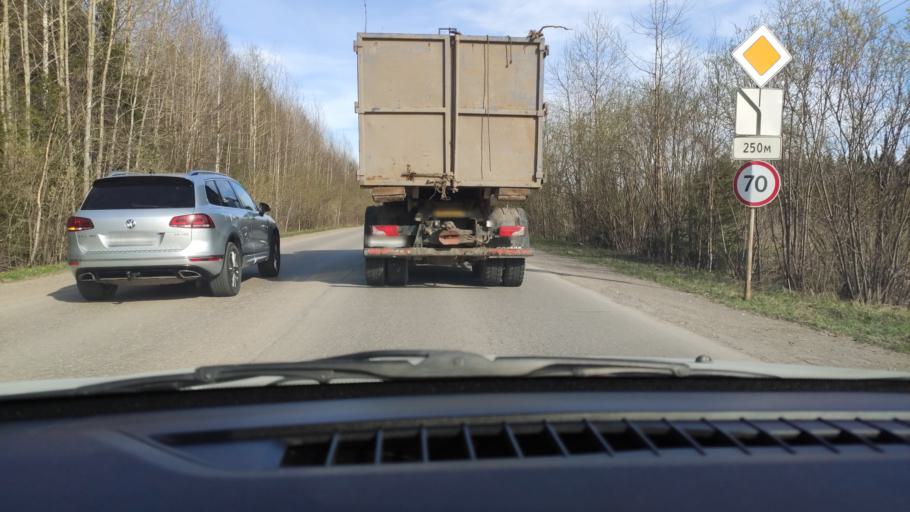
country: RU
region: Perm
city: Ferma
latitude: 57.9347
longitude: 56.4757
